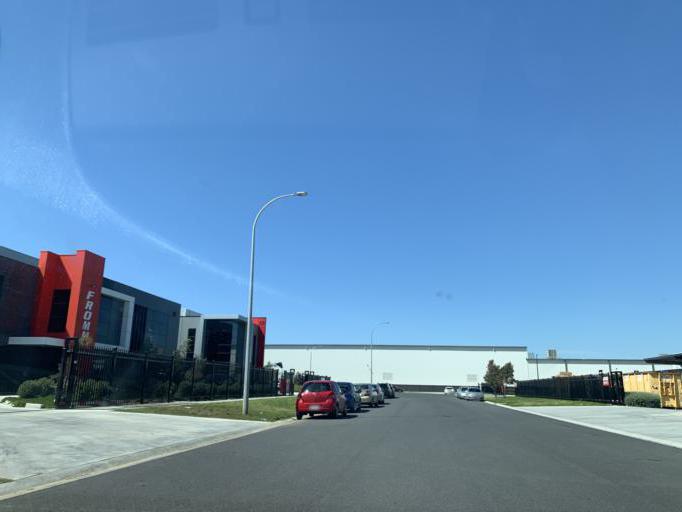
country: AU
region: Victoria
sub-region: Greater Dandenong
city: Keysborough
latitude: -38.0060
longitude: 145.1840
